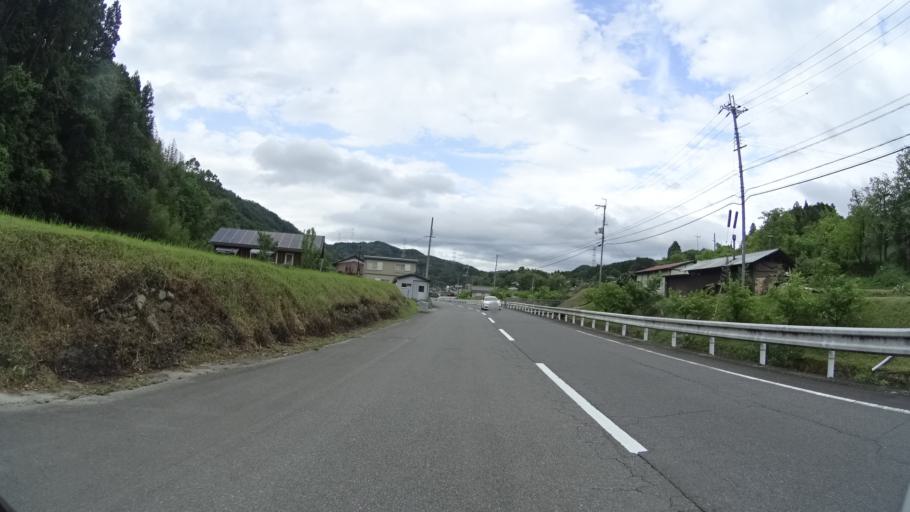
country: JP
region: Nara
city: Nara-shi
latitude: 34.7354
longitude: 135.9118
